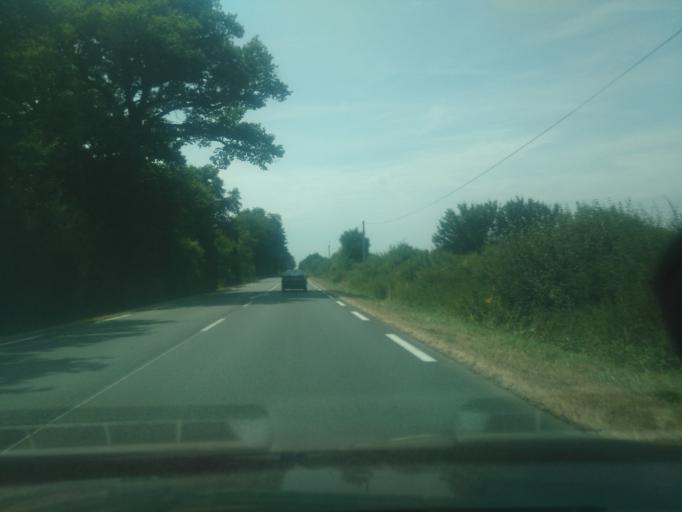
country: FR
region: Poitou-Charentes
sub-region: Departement des Deux-Sevres
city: Thenezay
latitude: 46.6562
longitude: -0.0628
